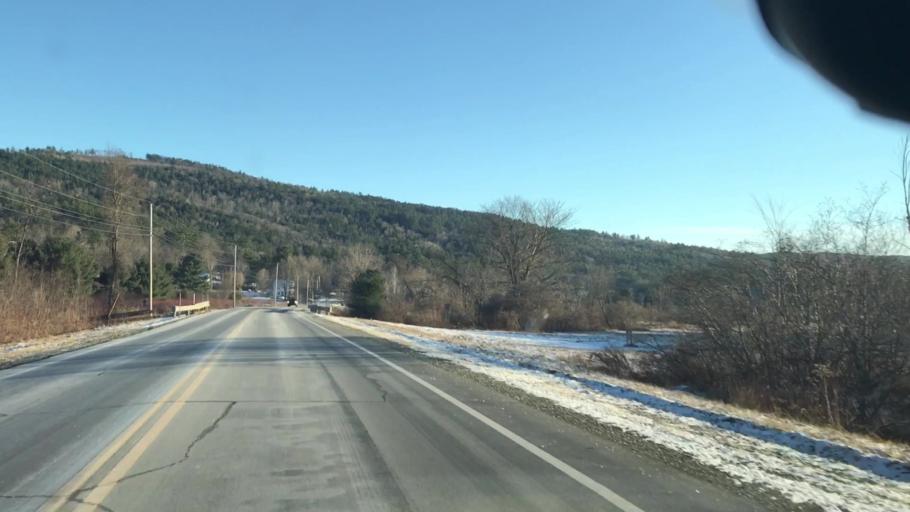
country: US
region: New Hampshire
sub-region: Grafton County
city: Lyme Town Offices
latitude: 43.8337
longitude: -72.1472
